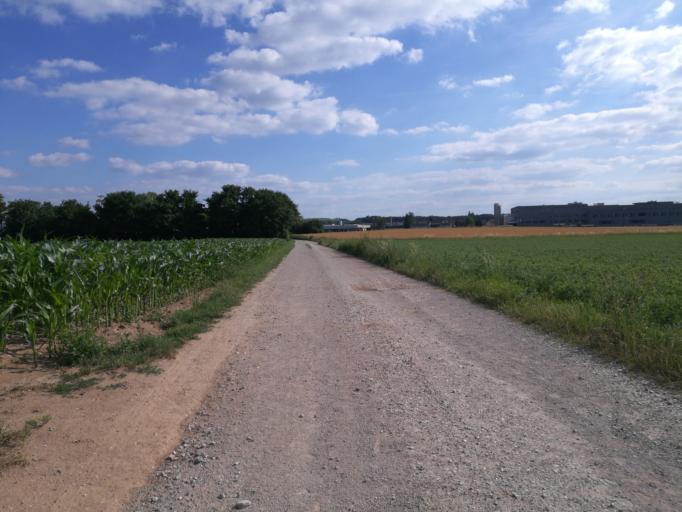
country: DE
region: Bavaria
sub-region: Regierungsbezirk Mittelfranken
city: Veitsbronn
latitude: 49.4977
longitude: 10.9179
